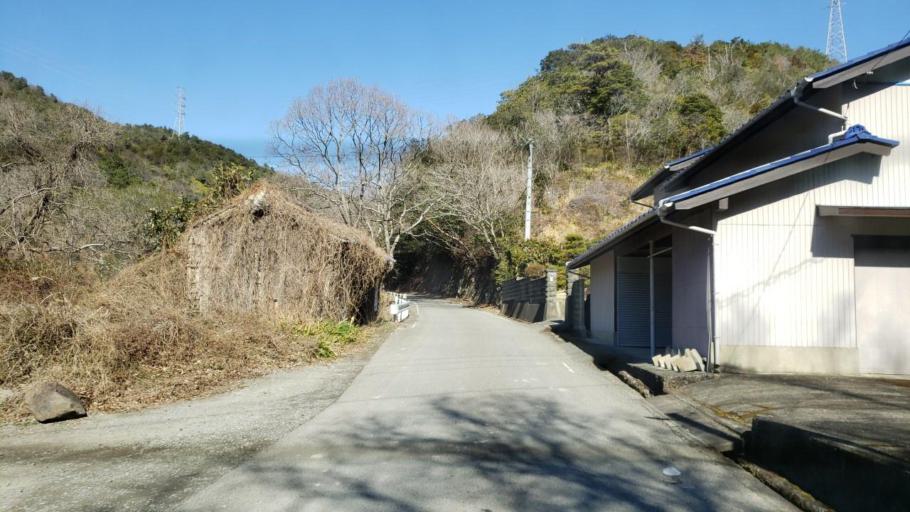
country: JP
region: Tokushima
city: Narutocho-mitsuishi
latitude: 34.1788
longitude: 134.5482
